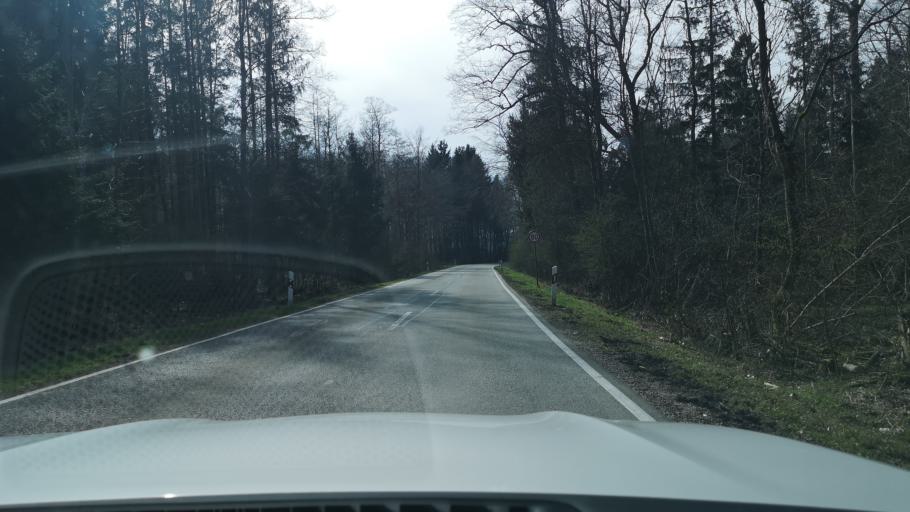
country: DE
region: Bavaria
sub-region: Upper Bavaria
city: Hohenlinden
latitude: 48.1598
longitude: 12.0143
